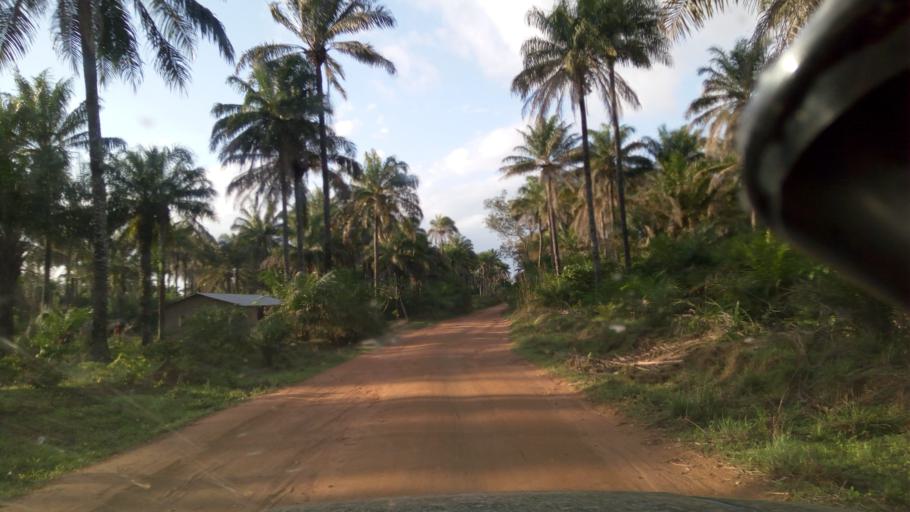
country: SL
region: Northern Province
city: Konakridee
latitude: 8.7668
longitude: -13.1406
